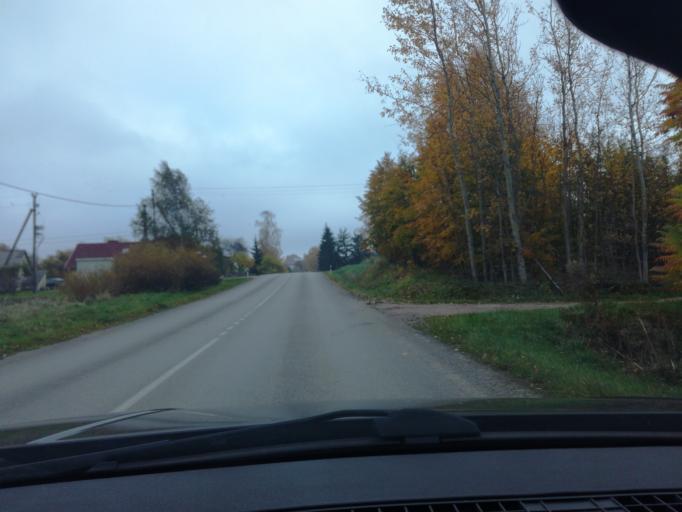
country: LT
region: Alytaus apskritis
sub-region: Alytus
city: Alytus
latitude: 54.4110
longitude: 23.9967
